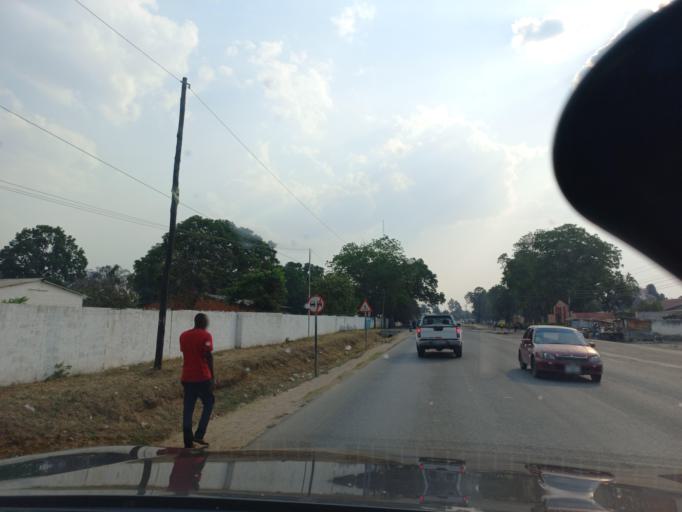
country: ZM
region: Lusaka
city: Lusaka
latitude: -15.4625
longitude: 28.2456
